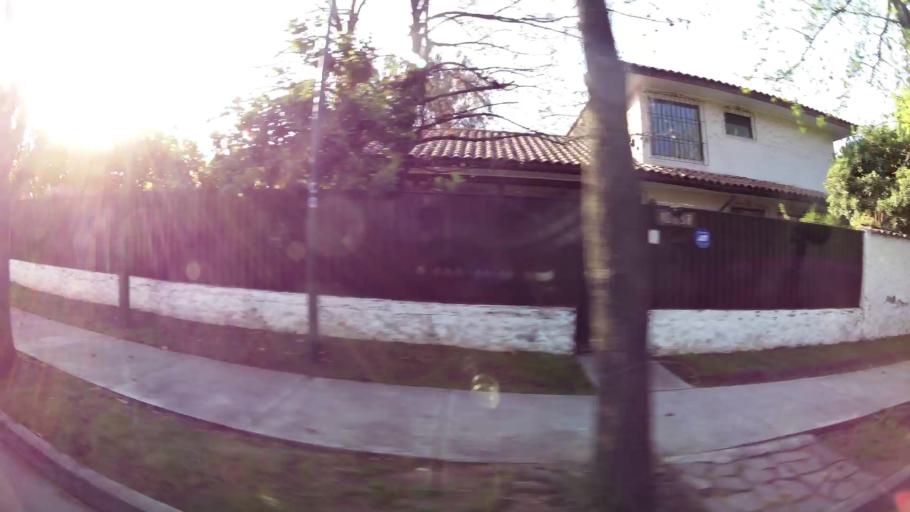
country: CL
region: Santiago Metropolitan
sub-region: Provincia de Santiago
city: Villa Presidente Frei, Nunoa, Santiago, Chile
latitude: -33.3459
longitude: -70.5421
